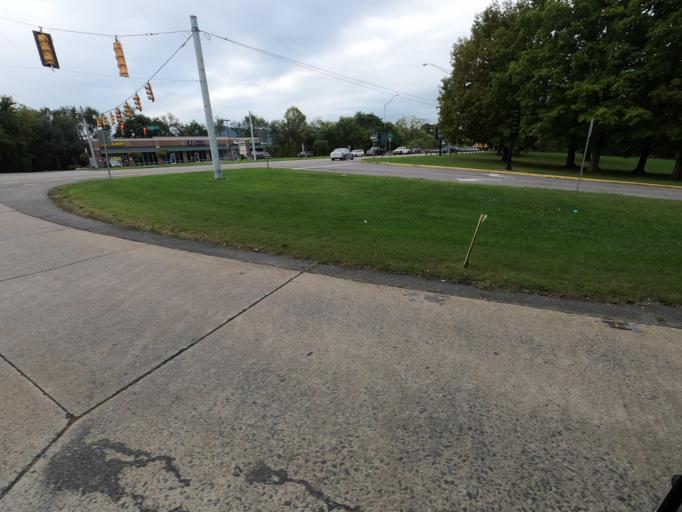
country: US
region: Tennessee
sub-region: Sullivan County
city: Kingsport
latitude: 36.5599
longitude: -82.5668
